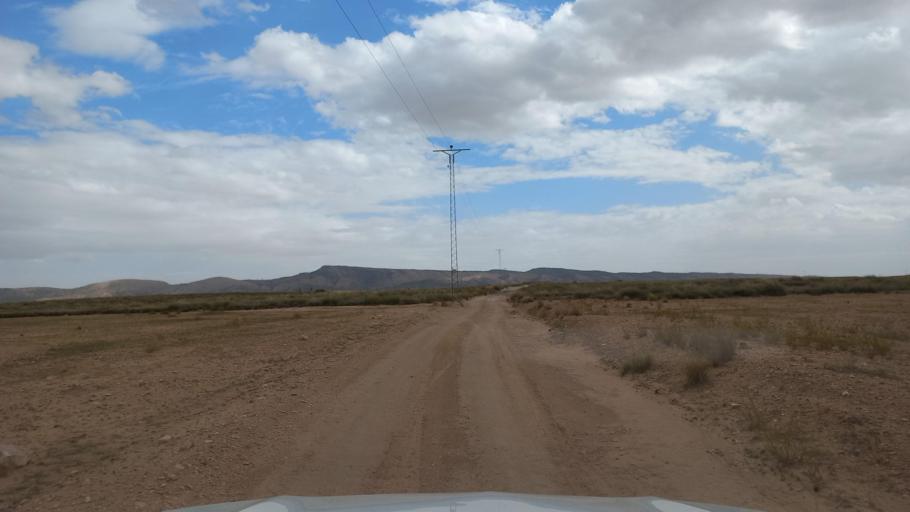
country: TN
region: Al Qasrayn
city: Sbiba
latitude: 35.3835
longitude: 9.1139
